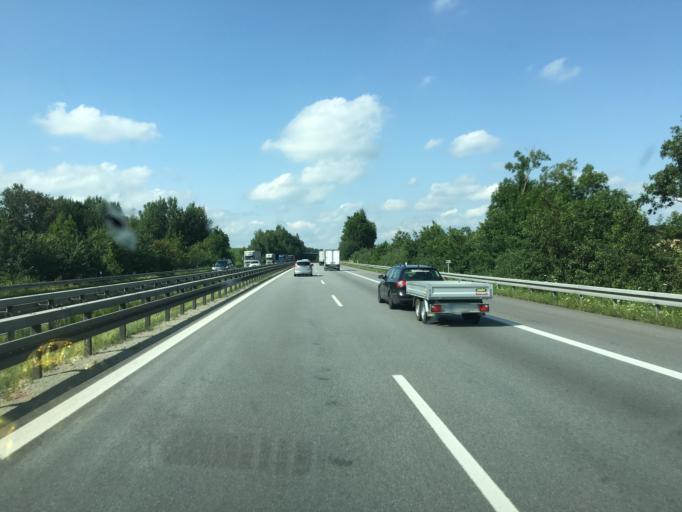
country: DE
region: Bavaria
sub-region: Lower Bavaria
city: Furstenzell
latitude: 48.4812
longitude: 13.3716
